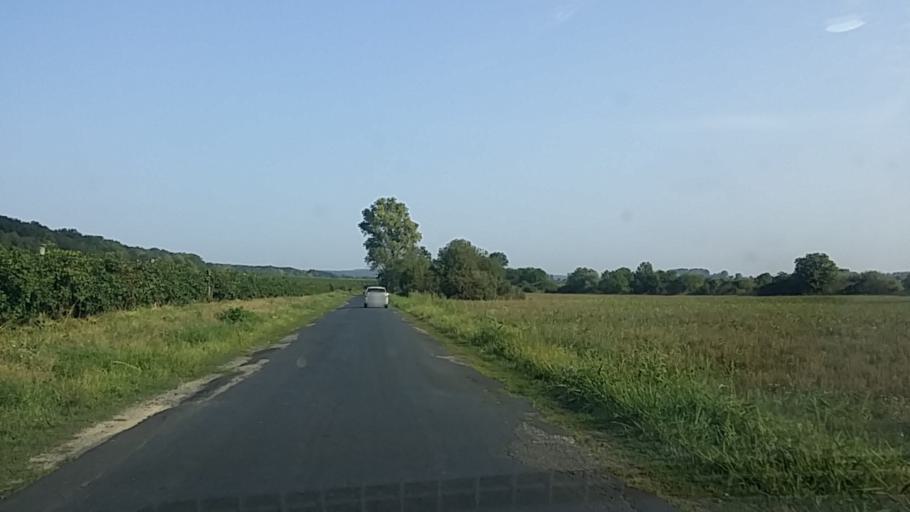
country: HU
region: Gyor-Moson-Sopron
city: Fertorakos
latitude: 47.6963
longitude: 16.6610
